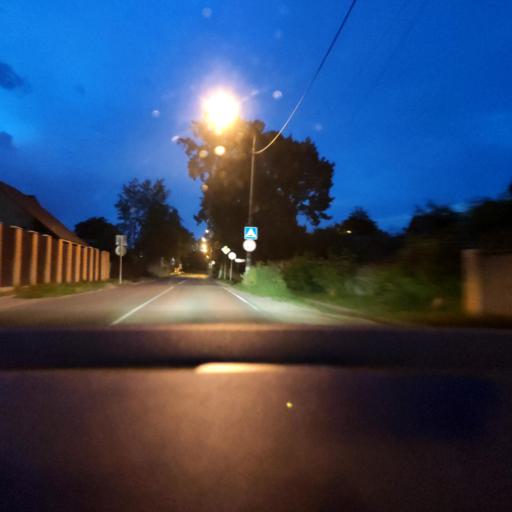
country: RU
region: Moskovskaya
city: Reutov
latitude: 55.7677
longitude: 37.8946
